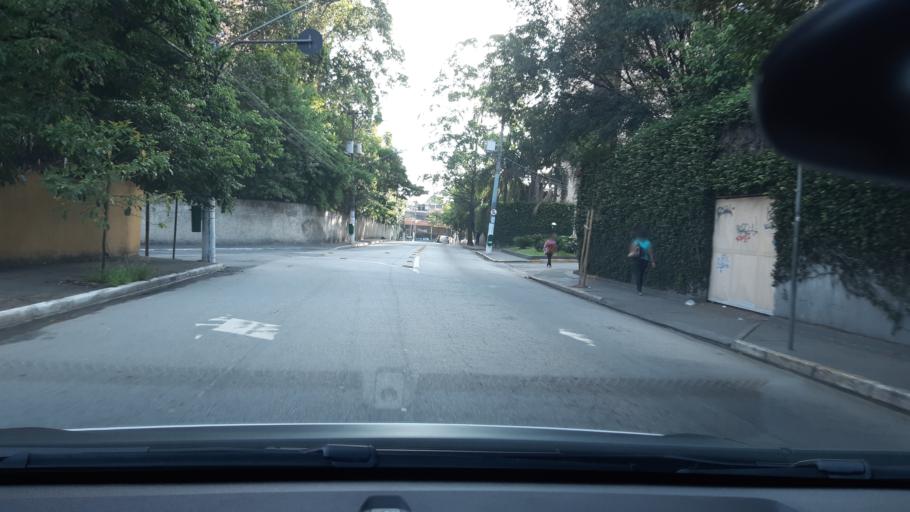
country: BR
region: Sao Paulo
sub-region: Sao Caetano Do Sul
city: Sao Caetano do Sul
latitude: -23.6304
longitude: -46.6037
